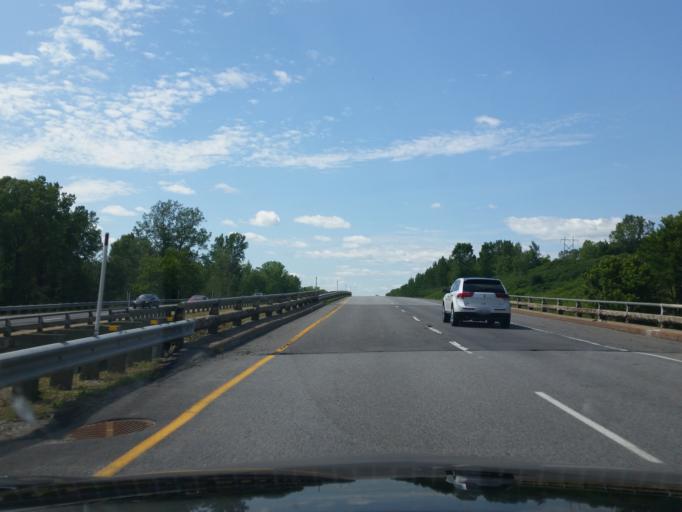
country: CA
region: Quebec
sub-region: Monteregie
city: Hudson
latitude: 45.4438
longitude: -74.1994
